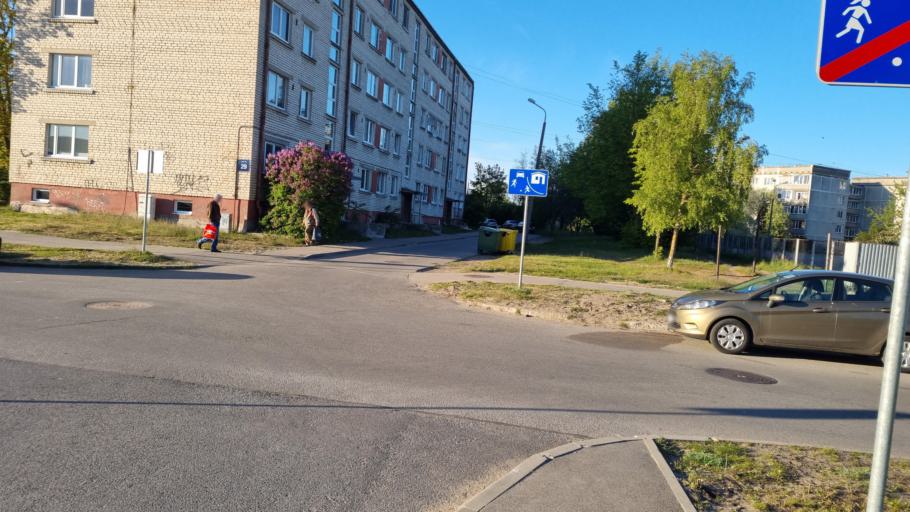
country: LV
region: Riga
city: Bolderaja
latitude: 57.0306
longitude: 24.0538
